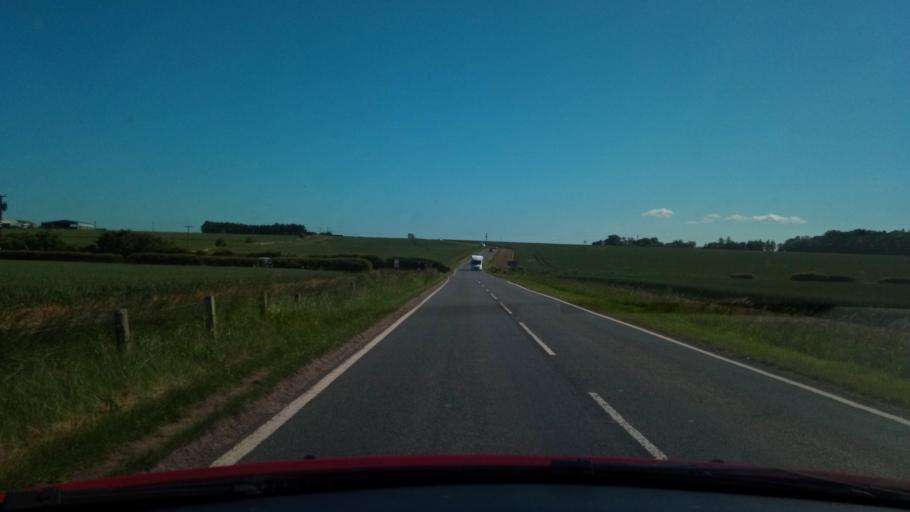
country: GB
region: Scotland
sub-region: East Lothian
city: North Berwick
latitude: 56.0549
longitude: -2.6593
